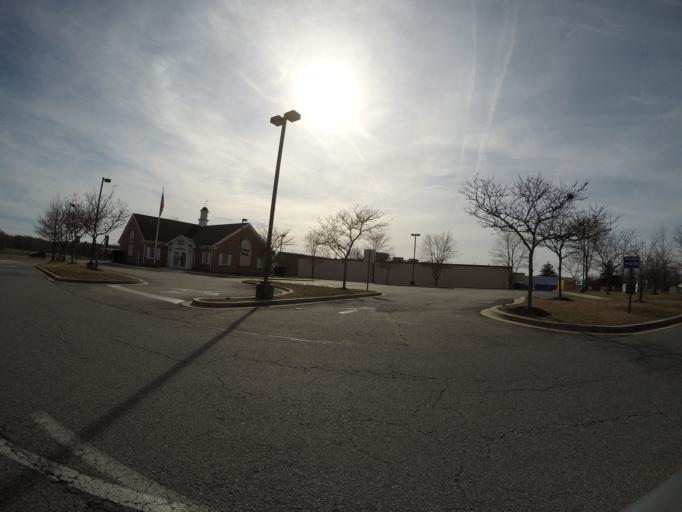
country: US
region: Maryland
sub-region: Cecil County
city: Elkton
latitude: 39.6034
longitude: -75.7994
